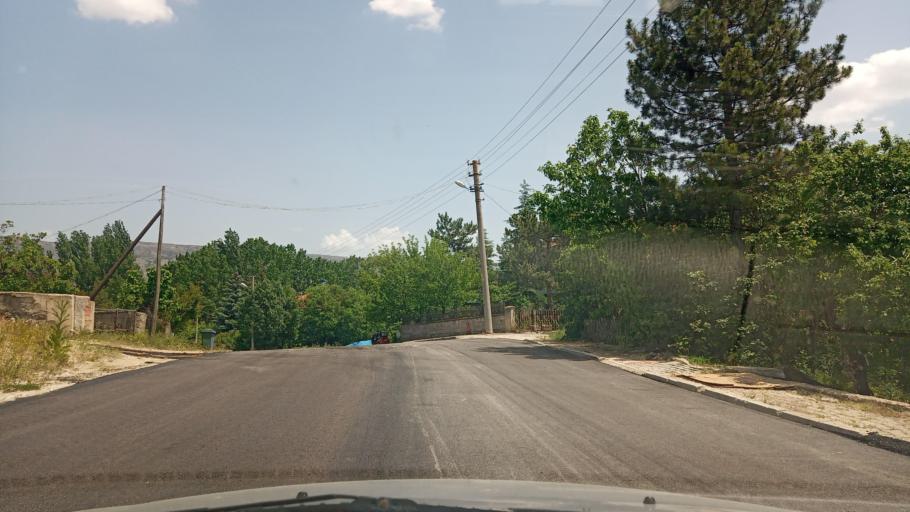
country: TR
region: Bolu
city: Seben
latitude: 40.4074
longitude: 31.5770
